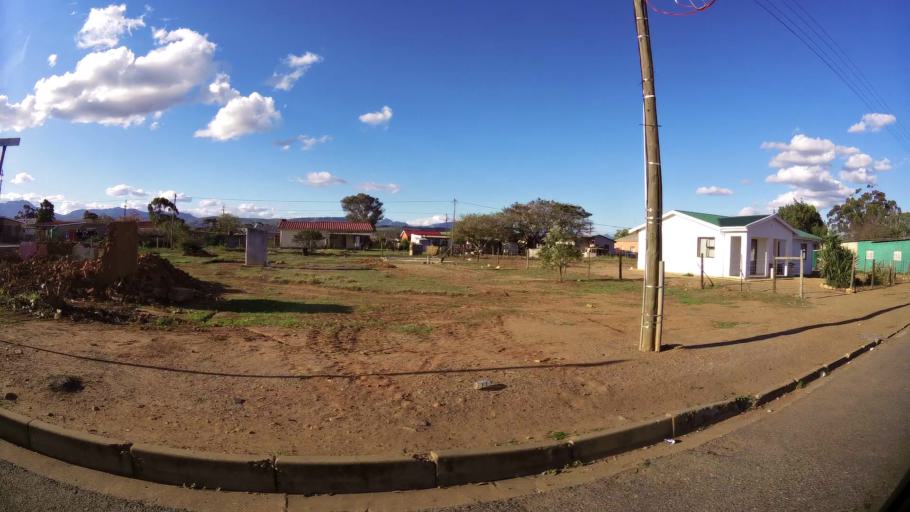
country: ZA
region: Western Cape
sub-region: Eden District Municipality
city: Riversdale
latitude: -34.1010
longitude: 20.9619
